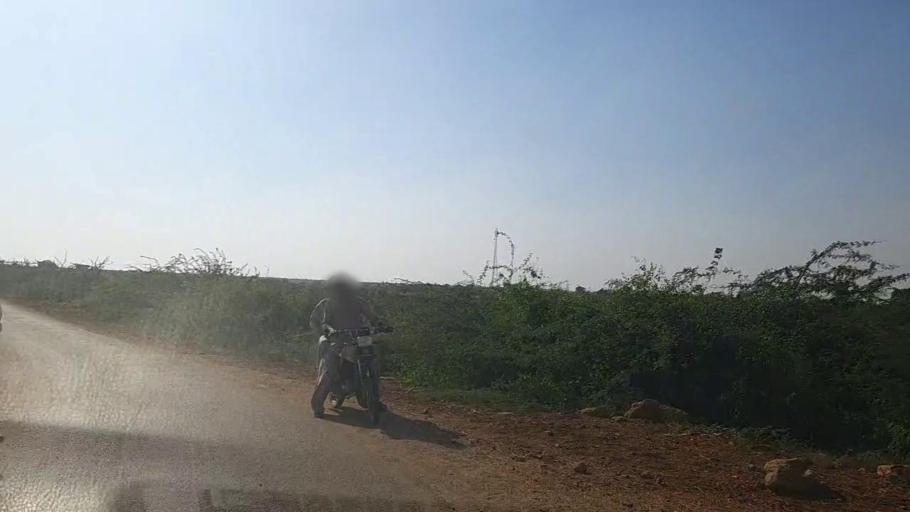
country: PK
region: Sindh
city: Daro Mehar
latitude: 25.0027
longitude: 68.1214
